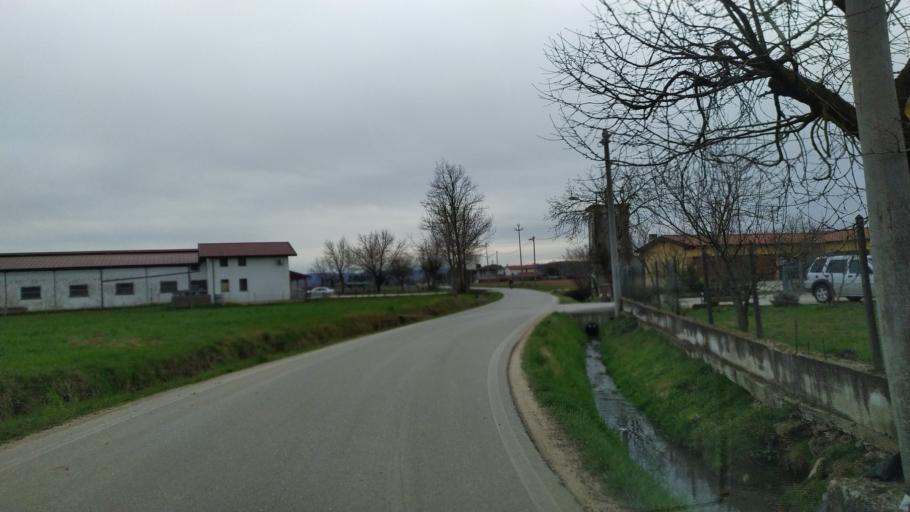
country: IT
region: Veneto
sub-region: Provincia di Vicenza
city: Crispi Cavour
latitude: 45.5837
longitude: 11.5178
